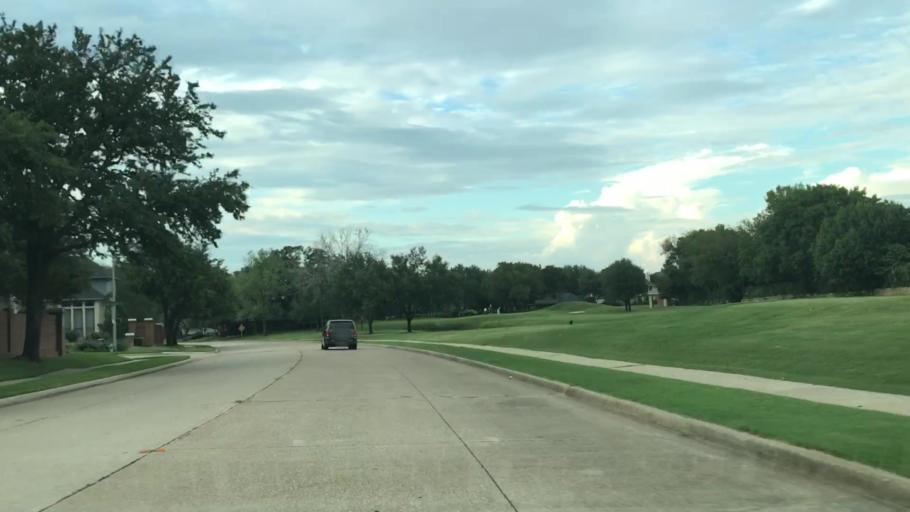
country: US
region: Texas
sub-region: Denton County
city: The Colony
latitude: 33.0358
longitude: -96.8461
